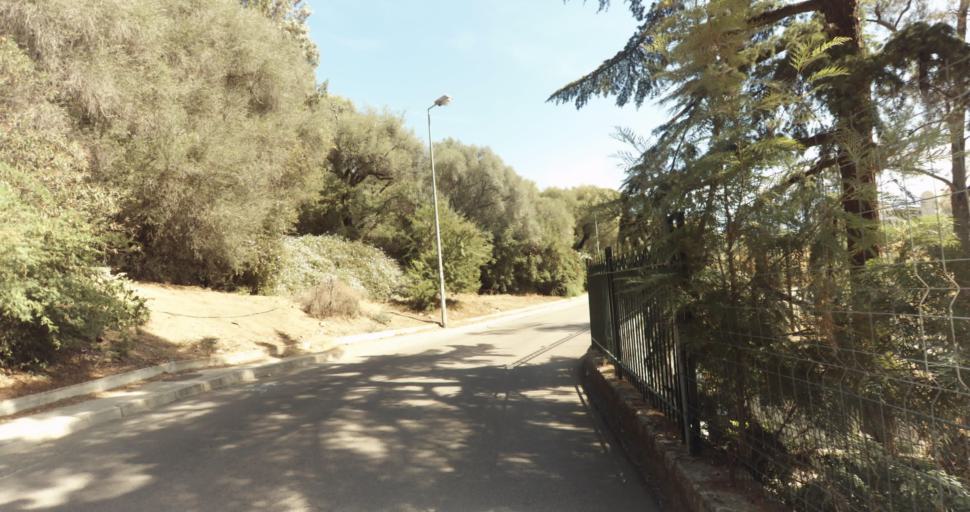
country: FR
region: Corsica
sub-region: Departement de la Corse-du-Sud
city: Ajaccio
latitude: 41.9169
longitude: 8.7237
